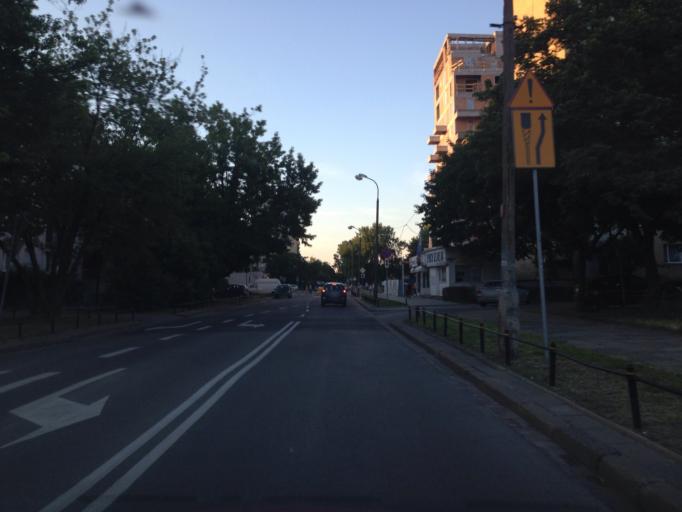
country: PL
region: Masovian Voivodeship
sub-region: Warszawa
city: Bielany
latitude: 52.2697
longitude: 20.9541
